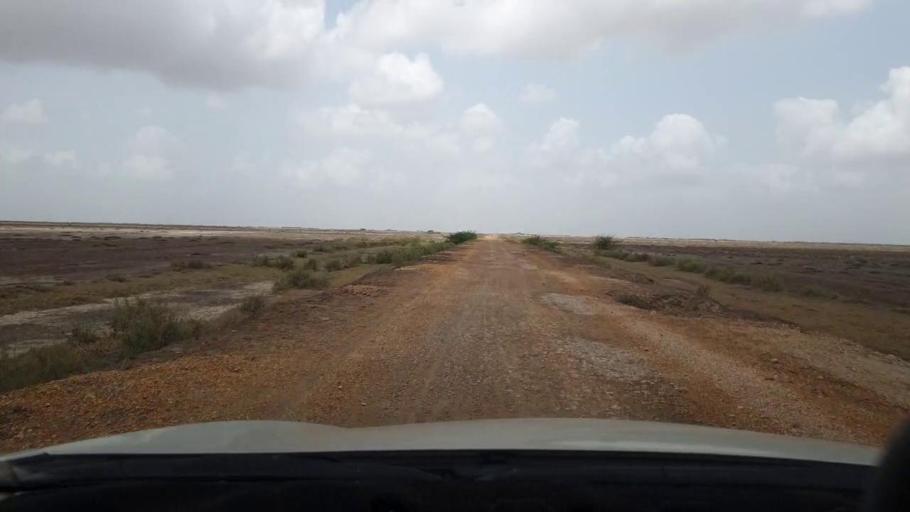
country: PK
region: Sindh
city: Kadhan
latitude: 24.3602
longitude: 68.8354
